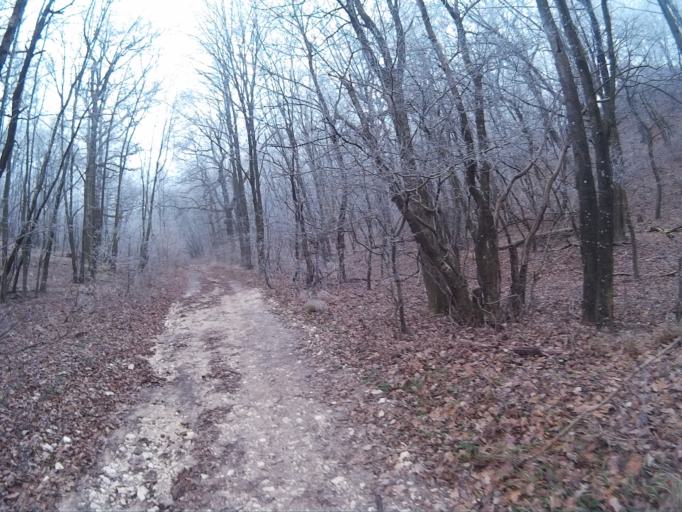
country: HU
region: Fejer
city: Zamoly
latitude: 47.3943
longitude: 18.3512
